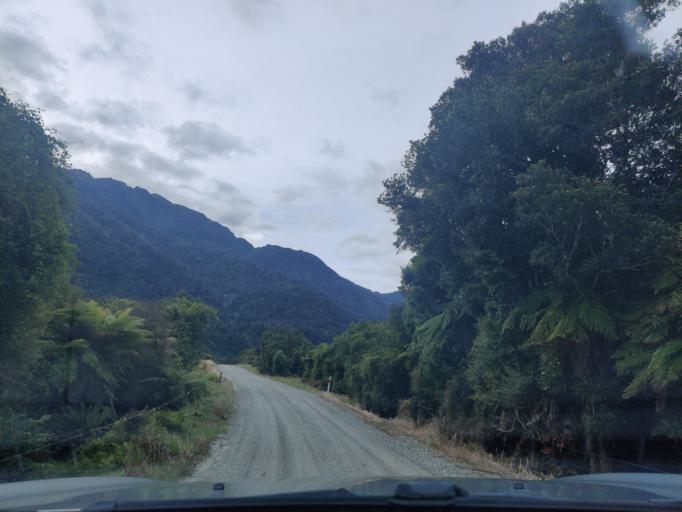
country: NZ
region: West Coast
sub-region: Westland District
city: Hokitika
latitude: -43.2925
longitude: 170.4060
